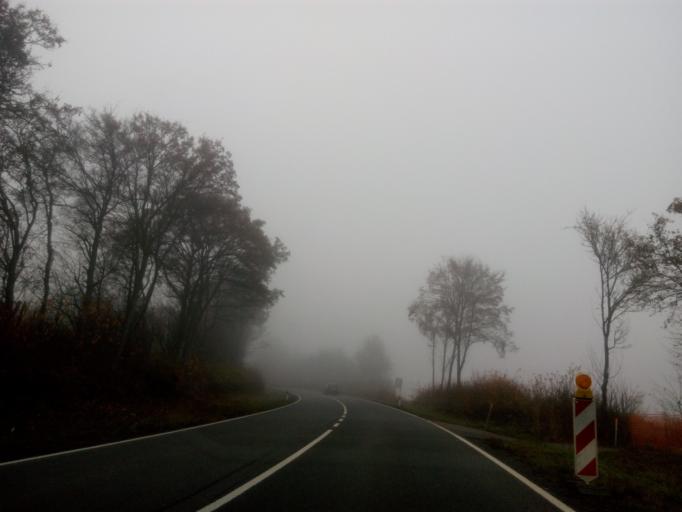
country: DE
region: Rheinland-Pfalz
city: Sien
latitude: 49.6880
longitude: 7.5161
